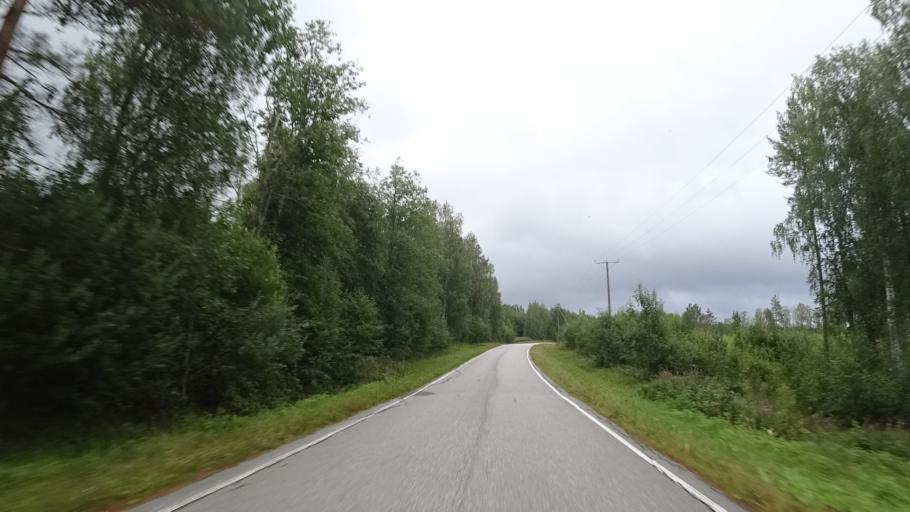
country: FI
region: North Karelia
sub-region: Joensuu
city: Ilomantsi
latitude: 63.2476
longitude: 30.7625
